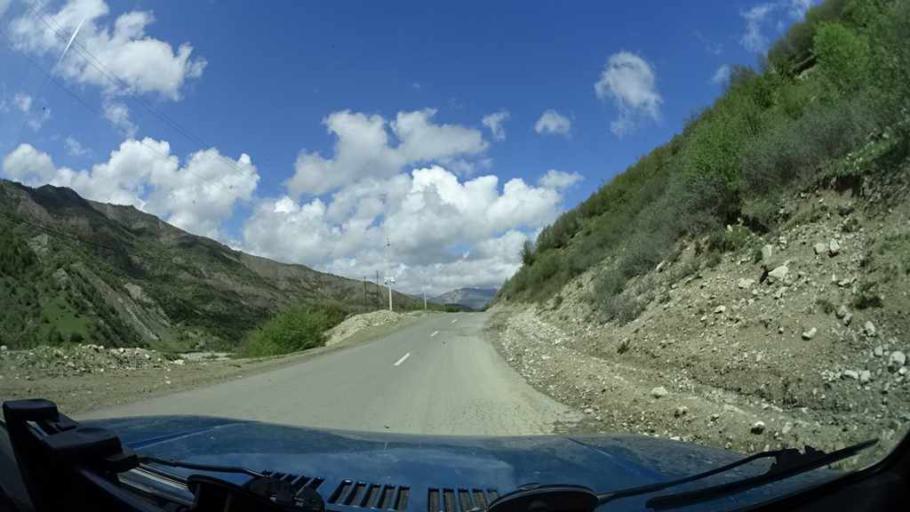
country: AZ
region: Ismayilli
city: Basqal
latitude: 40.8408
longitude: 48.3704
